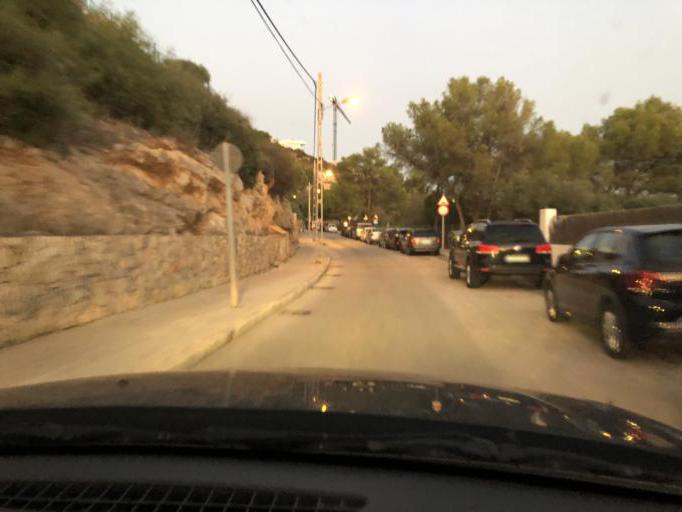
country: ES
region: Balearic Islands
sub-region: Illes Balears
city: Santa Ponsa
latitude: 39.5202
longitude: 2.4799
